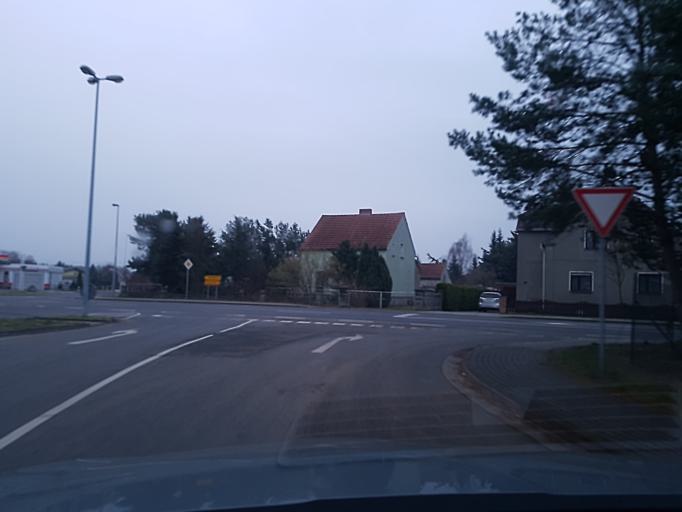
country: DE
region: Brandenburg
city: Doberlug-Kirchhain
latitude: 51.6267
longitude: 13.5804
